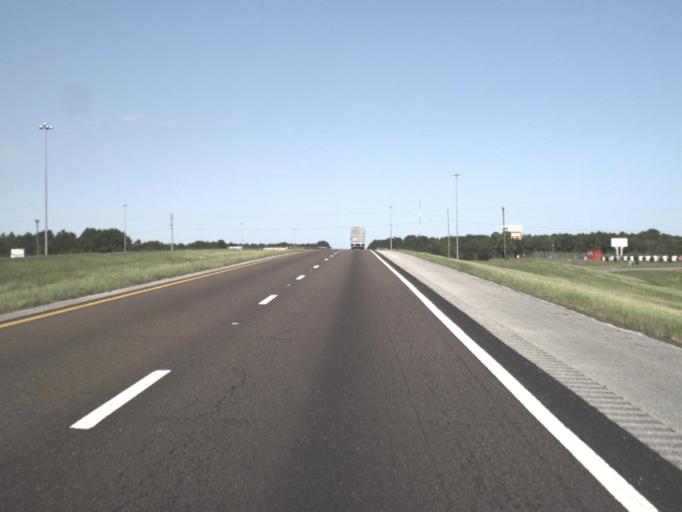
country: US
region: Florida
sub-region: Holmes County
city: Bonifay
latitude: 30.7628
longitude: -85.6819
